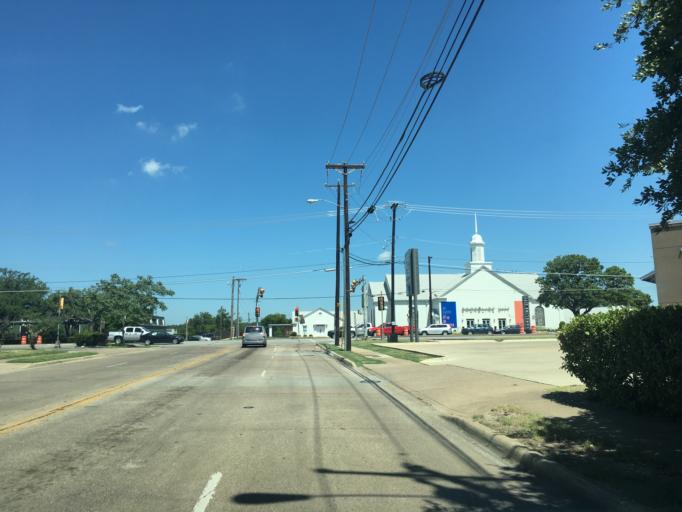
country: US
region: Texas
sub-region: Dallas County
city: Garland
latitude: 32.8439
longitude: -96.6886
